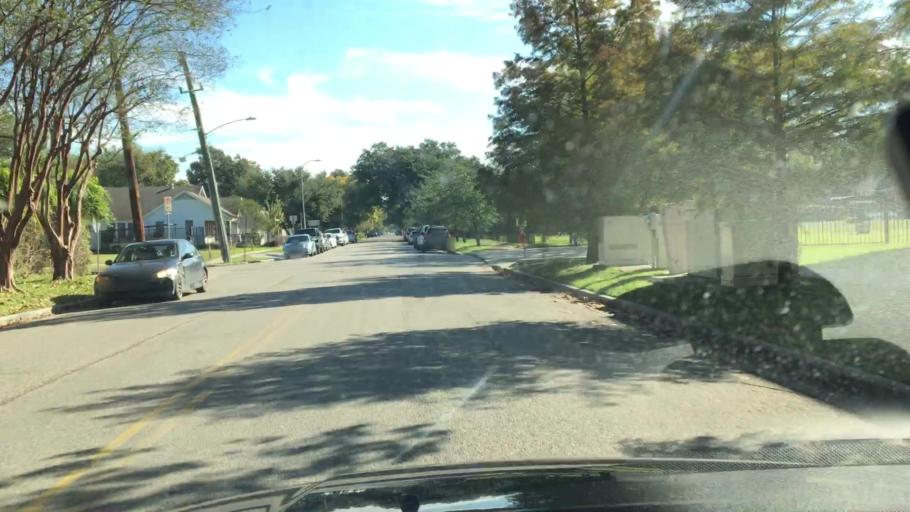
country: US
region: Texas
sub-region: Harris County
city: Houston
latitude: 29.7963
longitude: -95.3925
